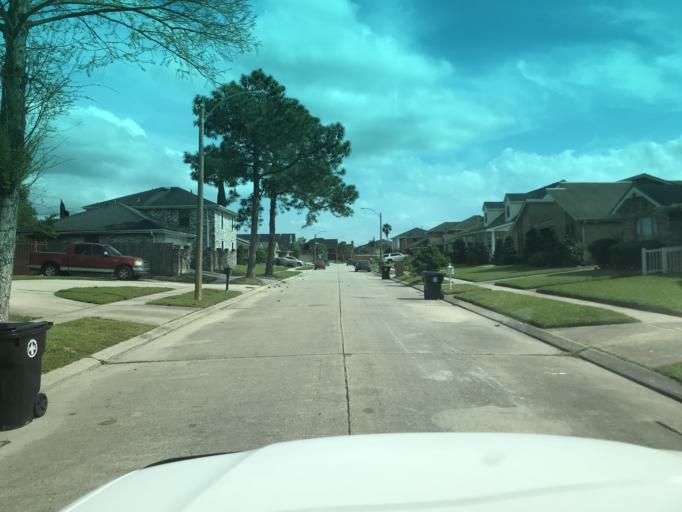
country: US
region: Louisiana
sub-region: Saint Bernard Parish
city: Chalmette
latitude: 30.0333
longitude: -89.9549
